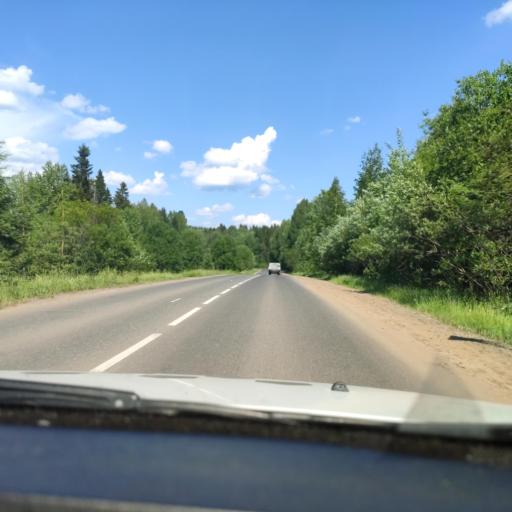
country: RU
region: Perm
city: Novyye Lyady
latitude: 58.1238
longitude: 56.4653
